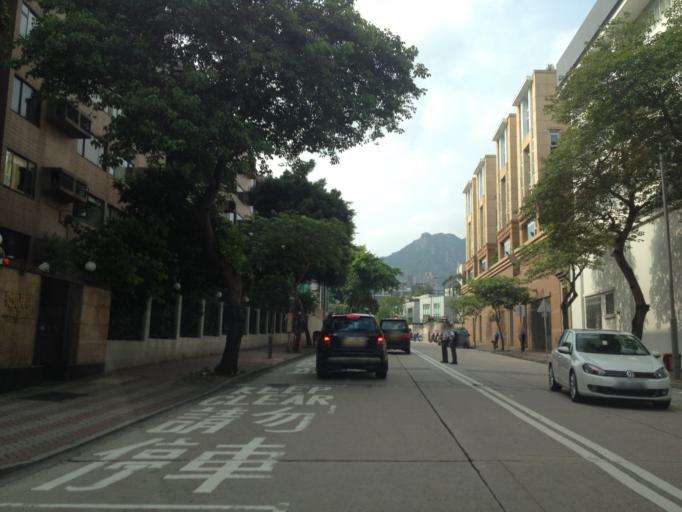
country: HK
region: Kowloon City
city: Kowloon
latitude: 22.3295
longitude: 114.1820
